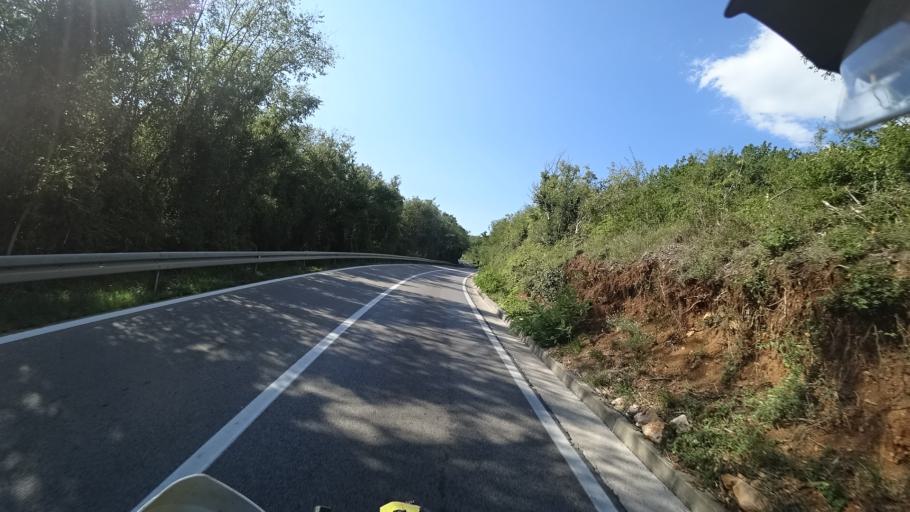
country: HR
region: Sibensko-Kniniska
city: Knin
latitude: 44.0223
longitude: 16.1958
